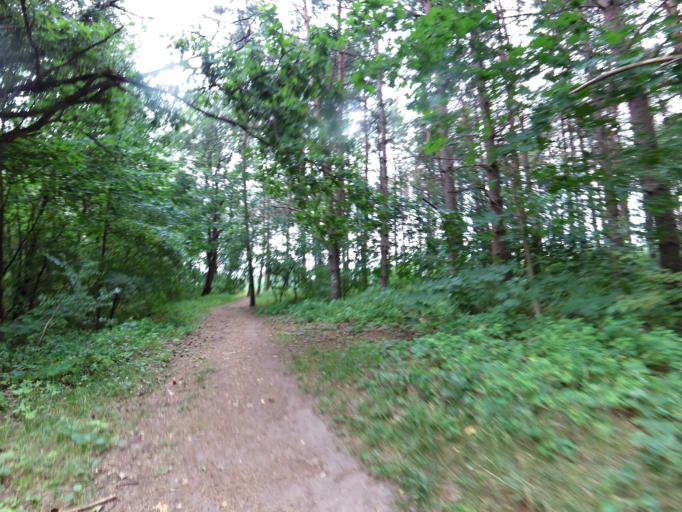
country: LT
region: Vilnius County
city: Lazdynai
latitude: 54.6855
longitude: 25.2130
